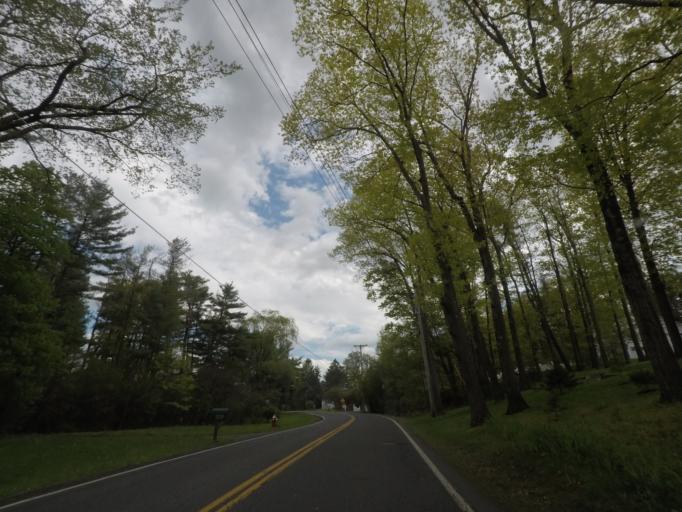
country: US
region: New York
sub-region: Albany County
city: Voorheesville
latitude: 42.6690
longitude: -73.9112
